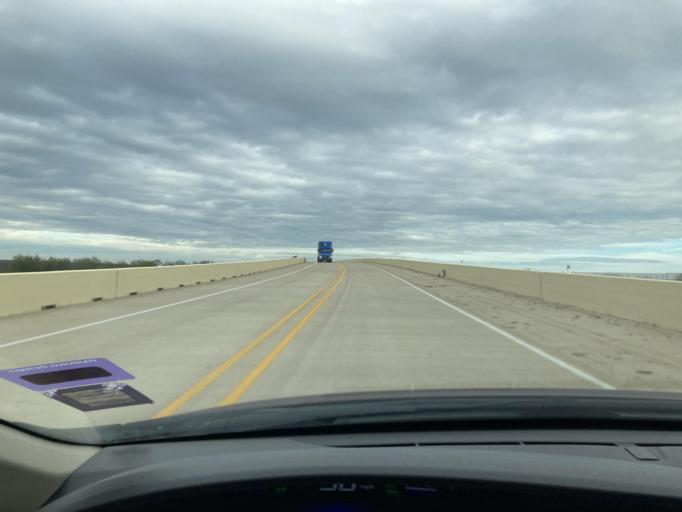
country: US
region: Texas
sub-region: Navarro County
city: Corsicana
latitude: 32.0408
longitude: -96.4558
